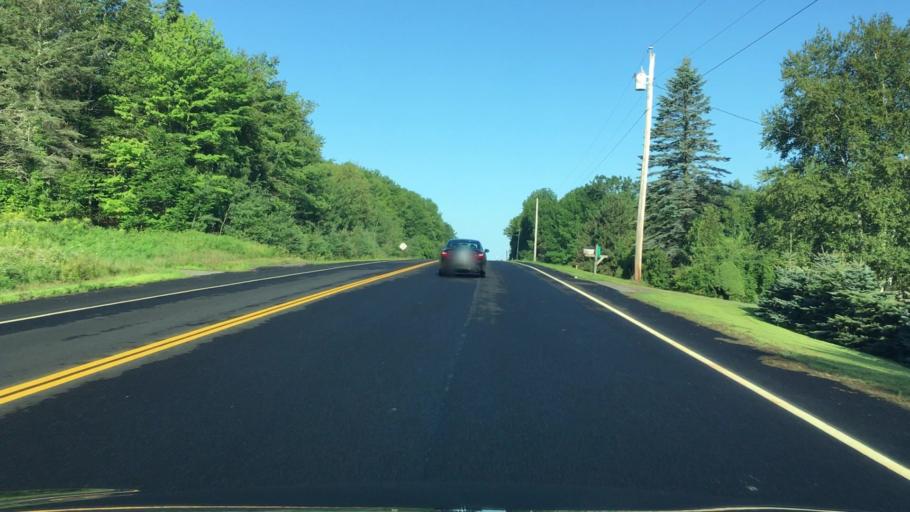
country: US
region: Maine
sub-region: Waldo County
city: Searsmont
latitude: 44.4001
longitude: -69.2493
